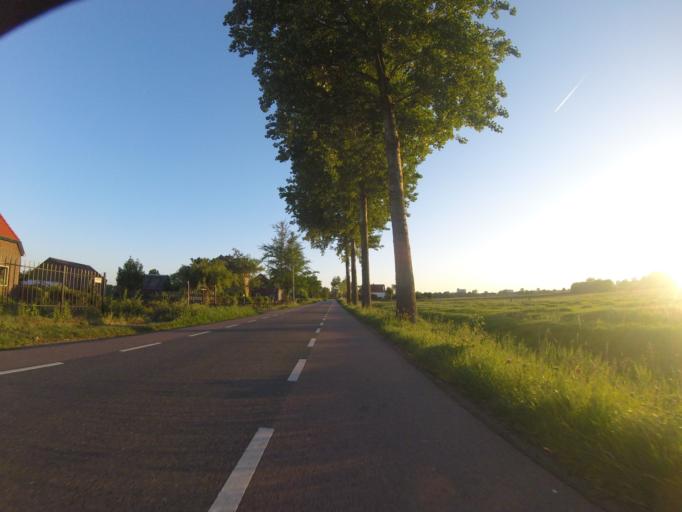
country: NL
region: North Holland
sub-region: Gemeente Haarlemmermeer
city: Hoofddorp
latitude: 52.3564
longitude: 4.6891
